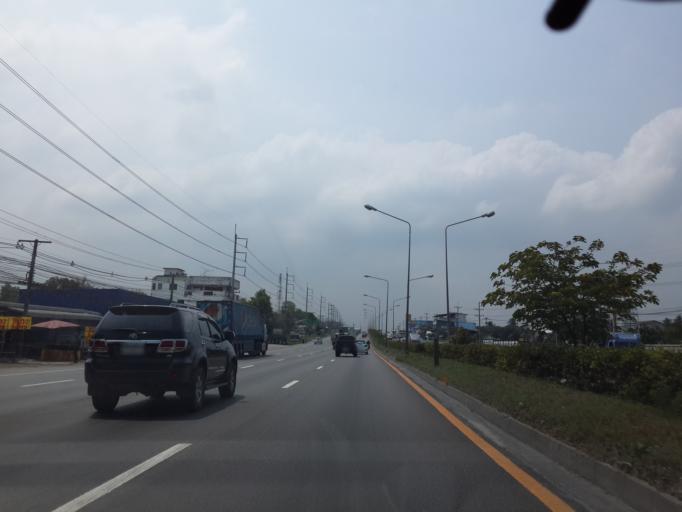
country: TH
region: Chon Buri
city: Chon Buri
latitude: 13.3712
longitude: 101.0191
